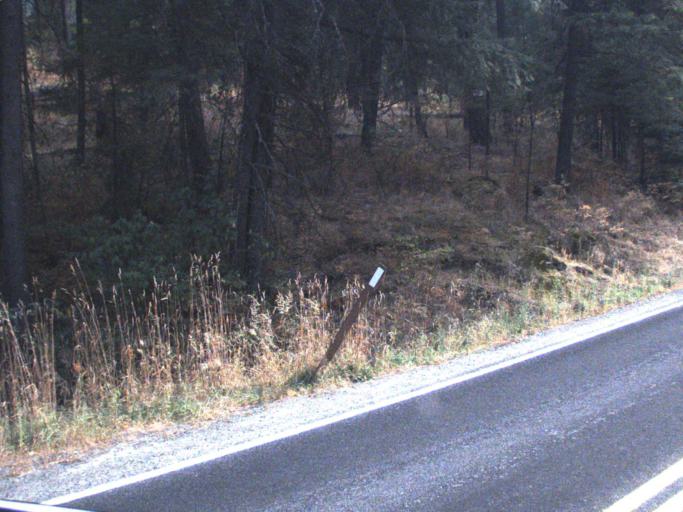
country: US
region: Washington
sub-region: Spokane County
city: Trentwood
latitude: 47.8295
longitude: -117.2028
